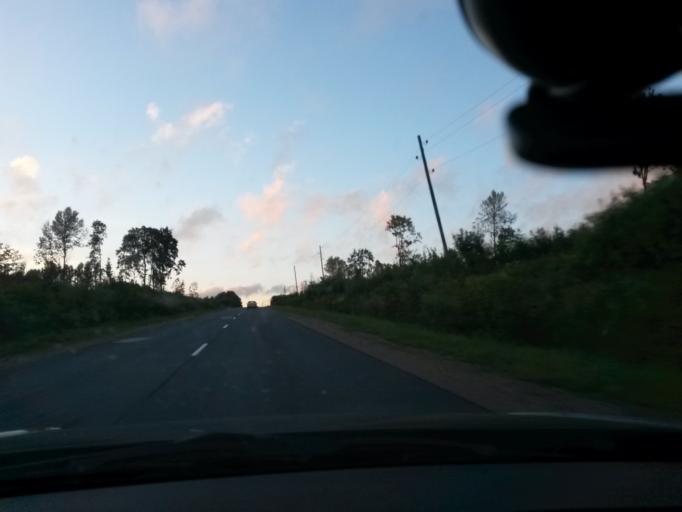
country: LV
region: Madonas Rajons
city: Madona
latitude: 56.7839
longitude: 26.0306
